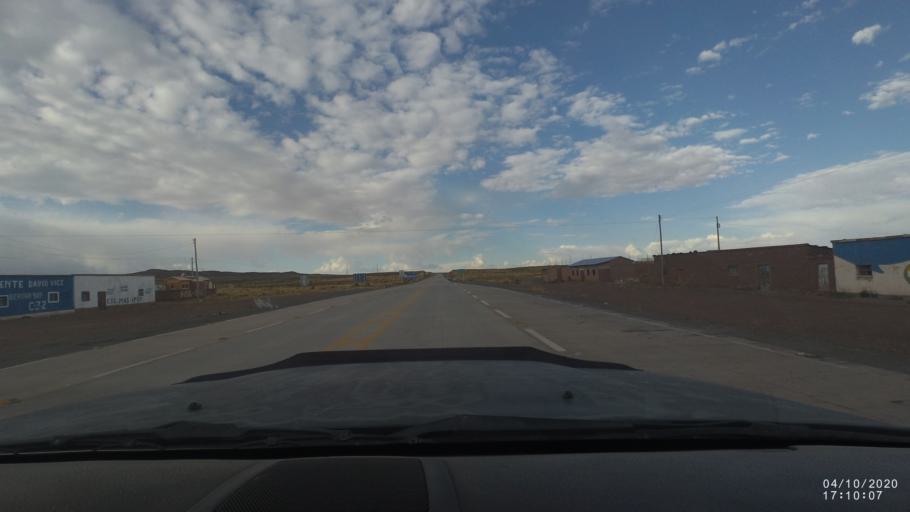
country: BO
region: Oruro
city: Oruro
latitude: -18.3351
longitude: -67.5869
